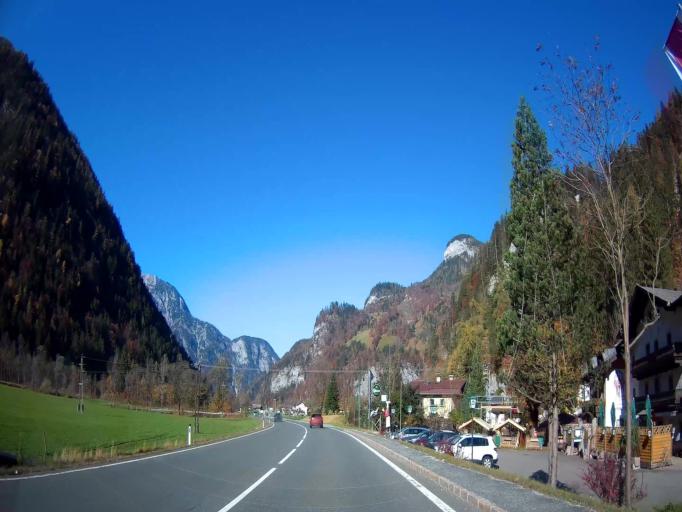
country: AT
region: Salzburg
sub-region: Politischer Bezirk Zell am See
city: Leogang
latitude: 47.5154
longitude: 12.7581
